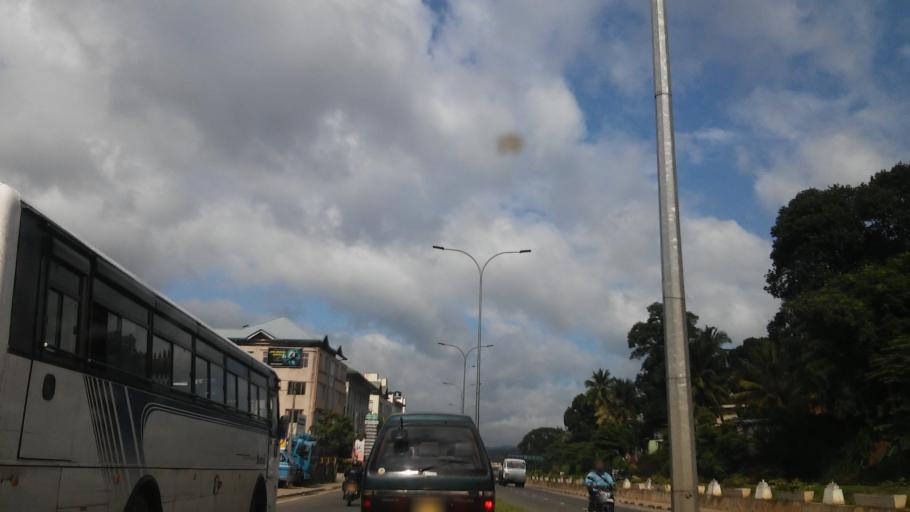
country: LK
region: Central
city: Kandy
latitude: 7.2750
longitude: 80.6140
